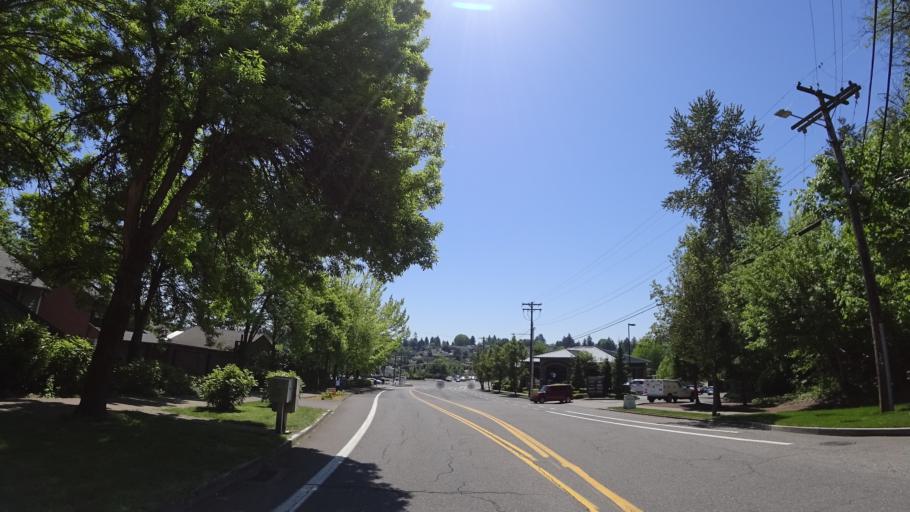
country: US
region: Oregon
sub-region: Multnomah County
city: Portland
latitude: 45.4723
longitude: -122.6855
